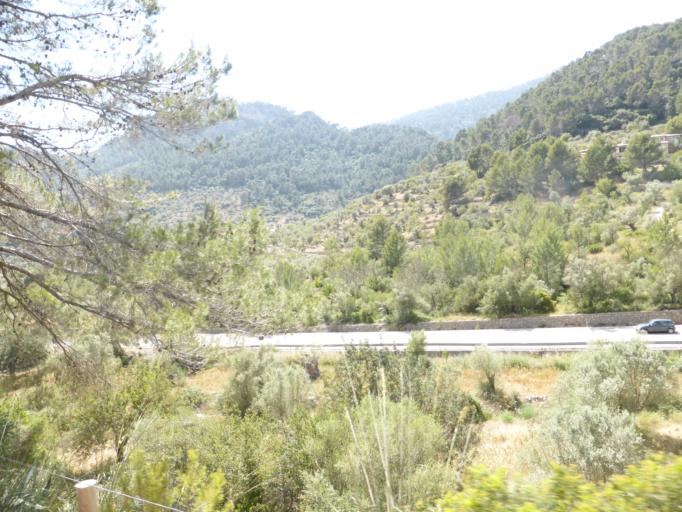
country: ES
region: Balearic Islands
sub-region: Illes Balears
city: Bunyola
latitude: 39.7122
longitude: 2.6909
